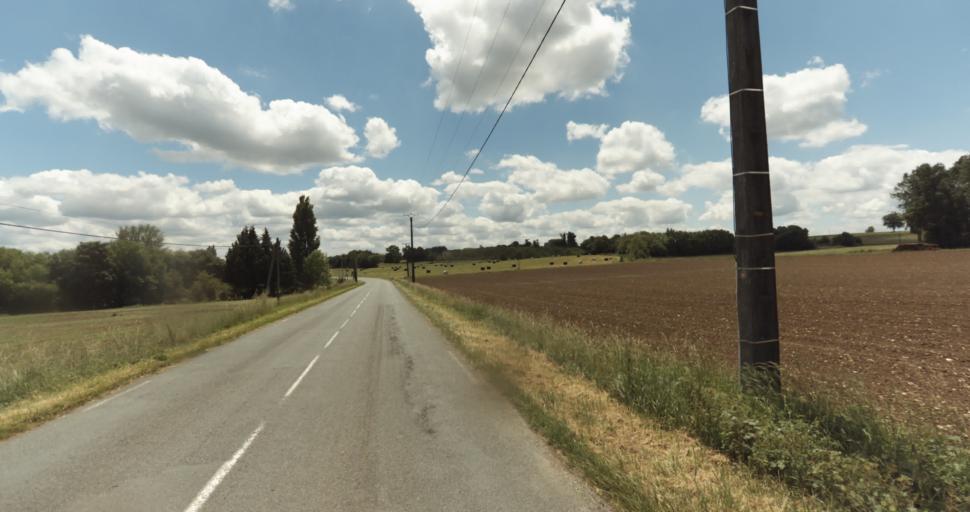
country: FR
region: Aquitaine
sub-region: Departement de la Dordogne
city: Beaumont-du-Perigord
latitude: 44.7206
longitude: 0.7948
